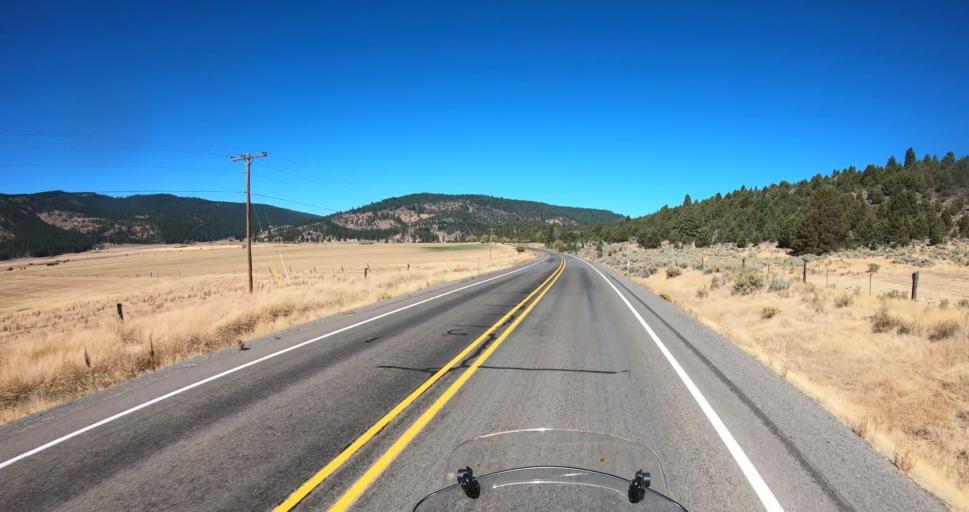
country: US
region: Oregon
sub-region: Lake County
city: Lakeview
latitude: 42.3735
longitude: -120.2977
